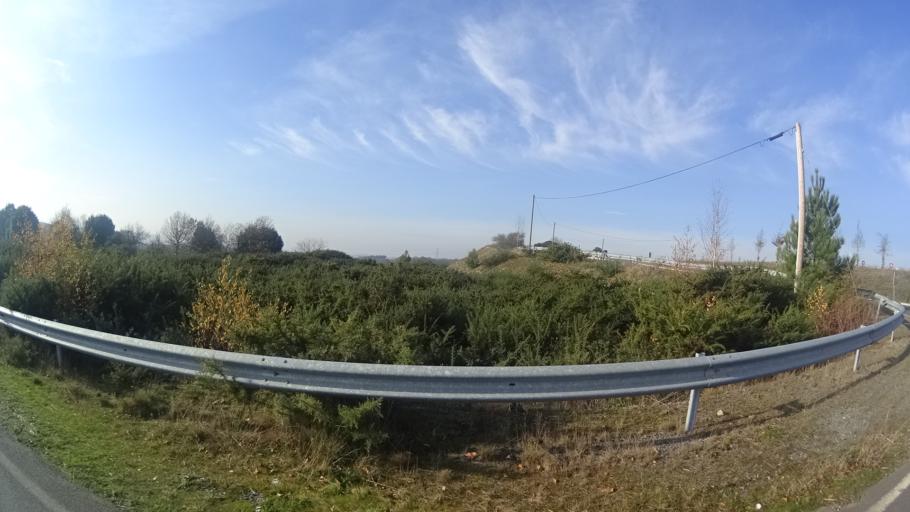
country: FR
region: Brittany
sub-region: Departement du Morbihan
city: Allaire
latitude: 47.6122
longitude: -2.1468
